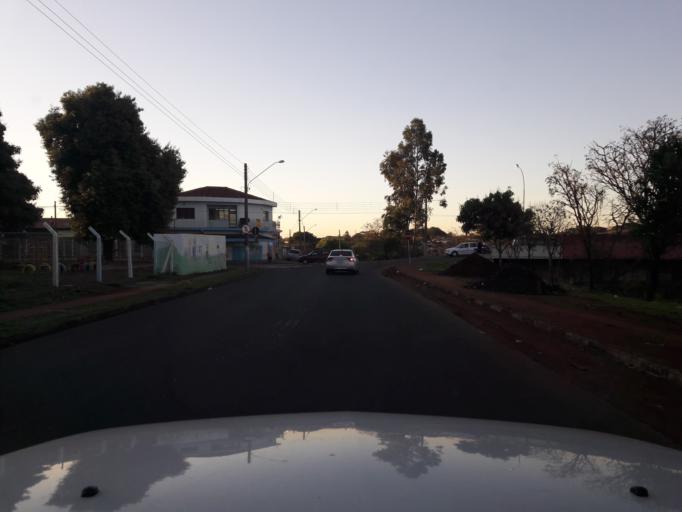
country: BR
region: Sao Paulo
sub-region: Moji-Guacu
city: Mogi-Gaucu
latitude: -22.3453
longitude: -46.9346
